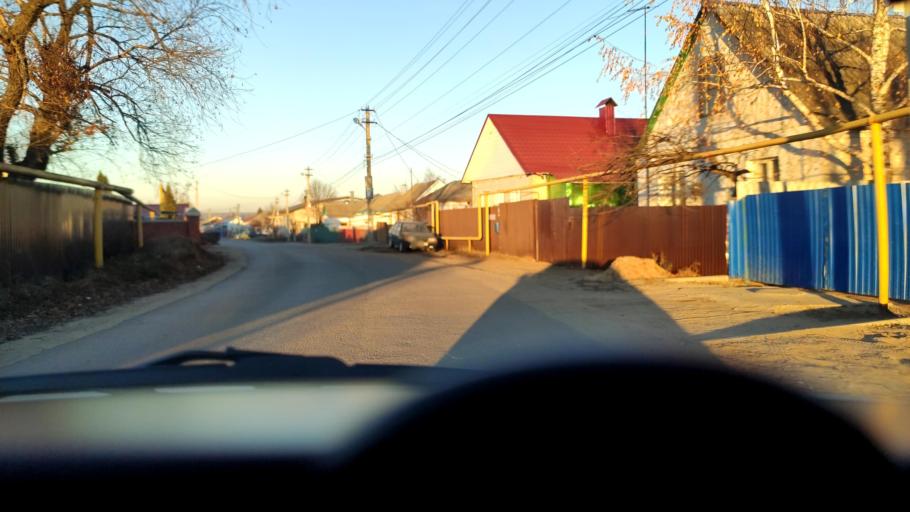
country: RU
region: Voronezj
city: Podgornoye
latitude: 51.7412
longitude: 39.1462
